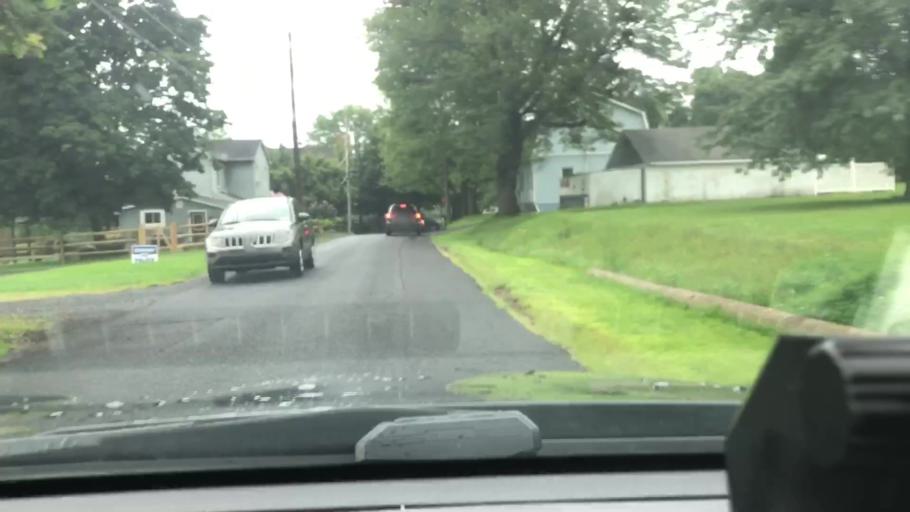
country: US
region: Pennsylvania
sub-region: Lehigh County
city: Coopersburg
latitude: 40.4856
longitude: -75.3953
